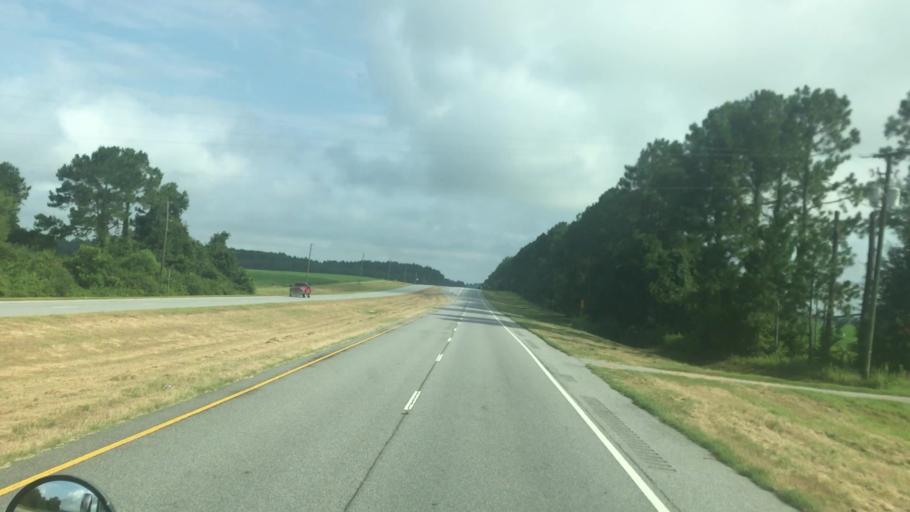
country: US
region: Georgia
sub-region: Miller County
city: Colquitt
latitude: 31.1885
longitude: -84.7639
